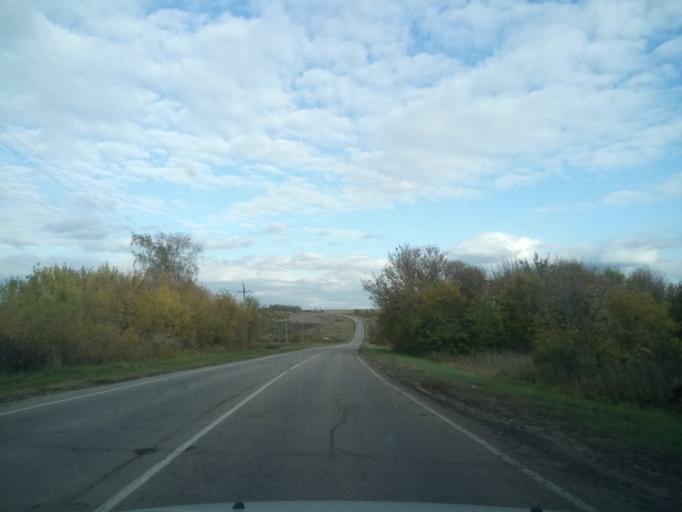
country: RU
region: Nizjnij Novgorod
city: Bol'shoye Boldino
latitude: 54.9642
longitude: 45.2281
